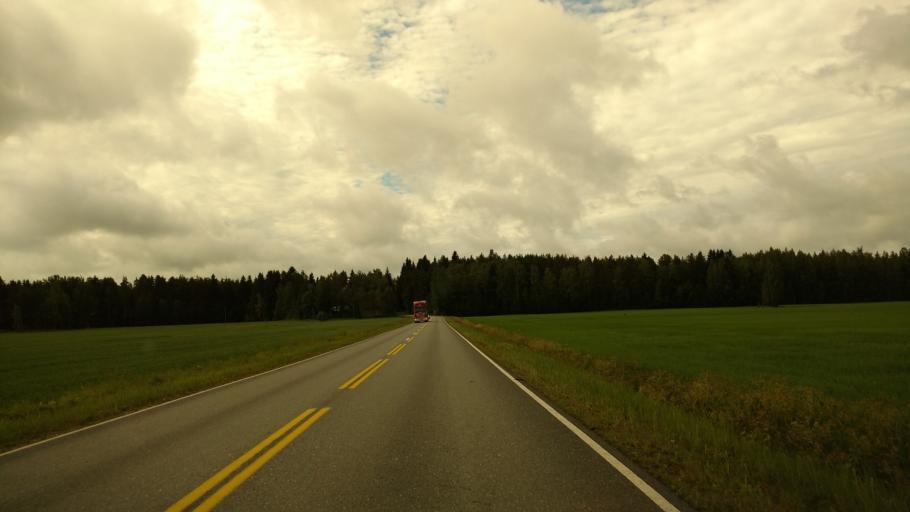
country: FI
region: Varsinais-Suomi
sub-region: Loimaa
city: Koski Tl
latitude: 60.6337
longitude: 23.1054
